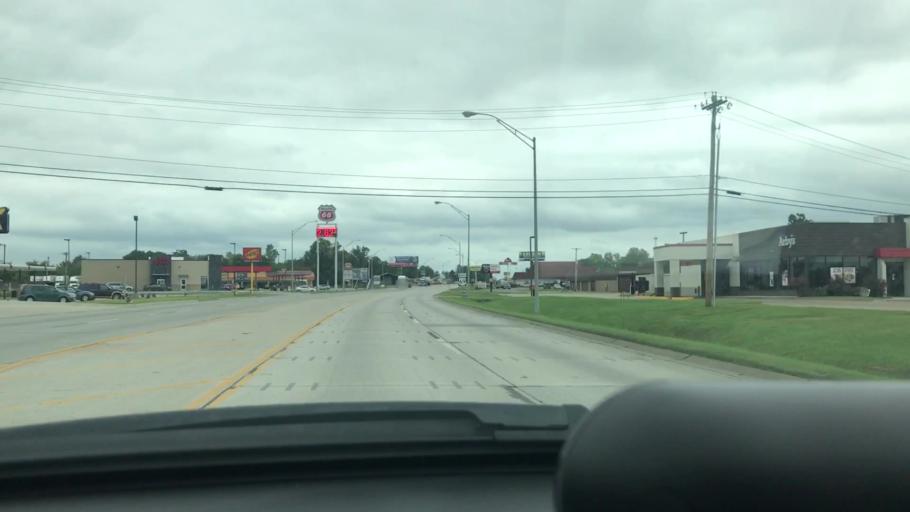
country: US
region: Oklahoma
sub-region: Wagoner County
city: Wagoner
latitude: 35.9600
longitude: -95.3946
